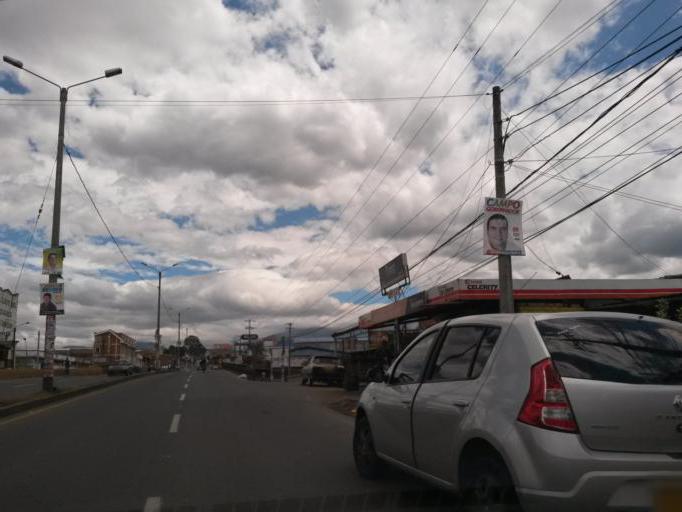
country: CO
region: Cauca
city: Popayan
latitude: 2.4813
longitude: -76.5705
